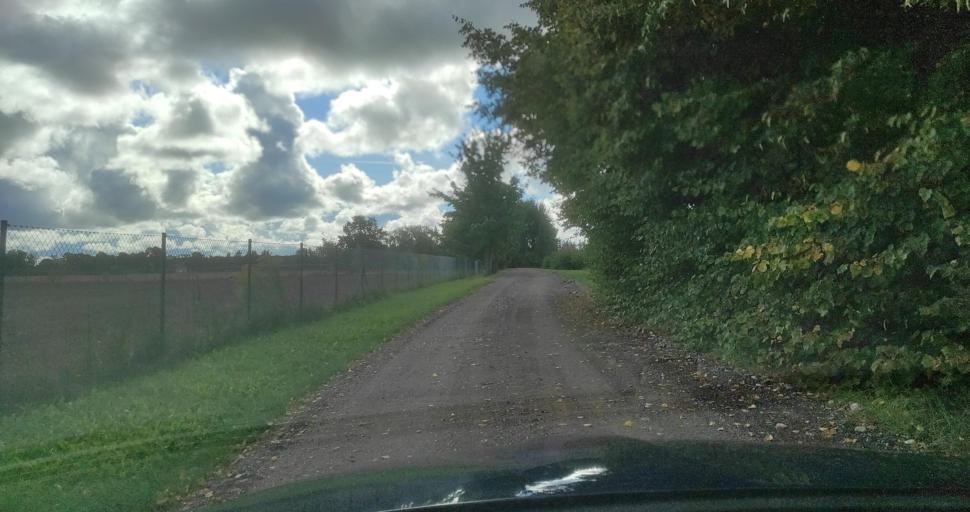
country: LV
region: Ventspils Rajons
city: Piltene
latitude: 57.2659
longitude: 21.6035
